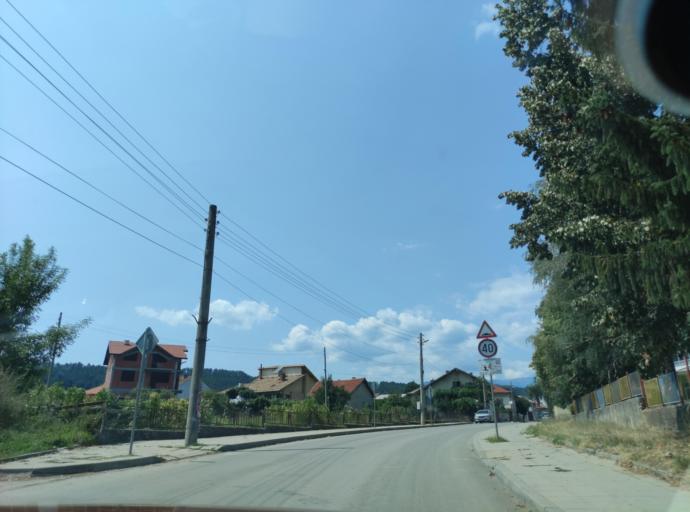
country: BG
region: Blagoevgrad
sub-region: Obshtina Belitsa
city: Belitsa
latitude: 41.9469
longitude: 23.5597
